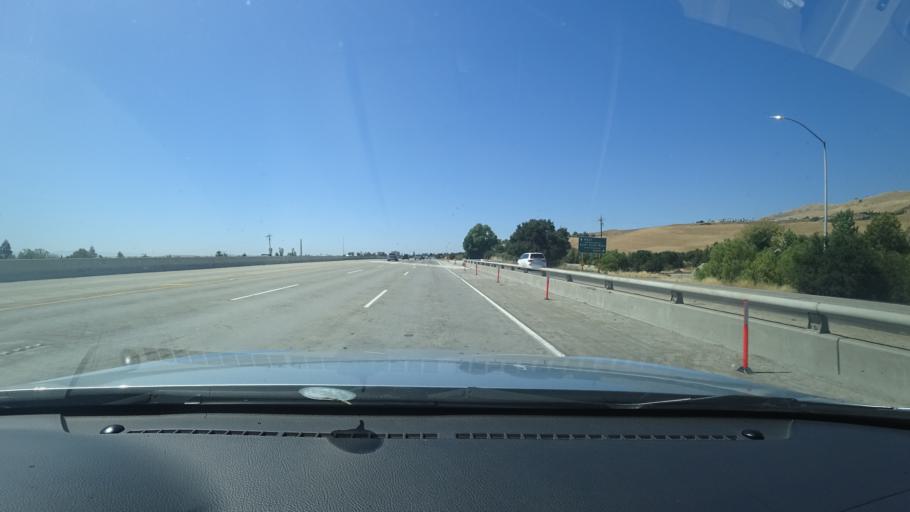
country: US
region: California
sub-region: Santa Clara County
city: Milpitas
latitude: 37.4652
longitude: -121.9044
